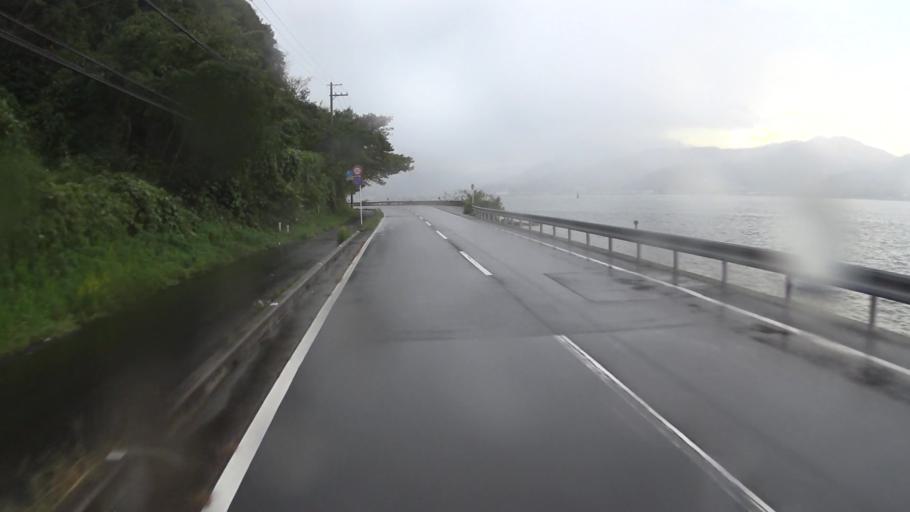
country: JP
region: Kyoto
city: Miyazu
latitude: 35.5568
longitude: 135.2043
